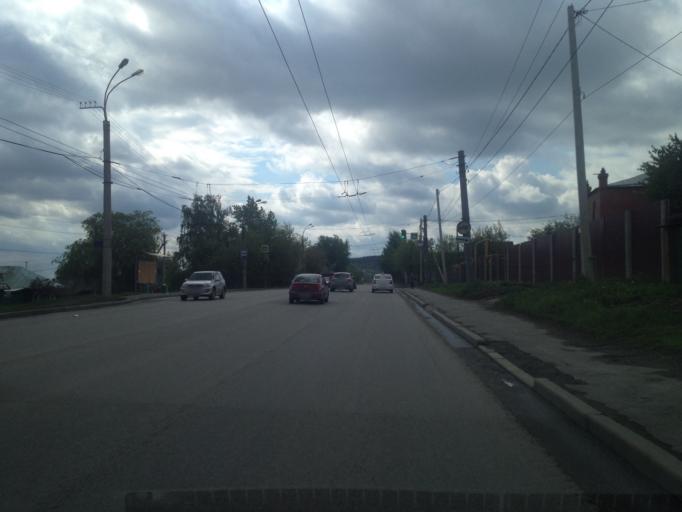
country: RU
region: Sverdlovsk
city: Istok
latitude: 56.7542
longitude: 60.6754
